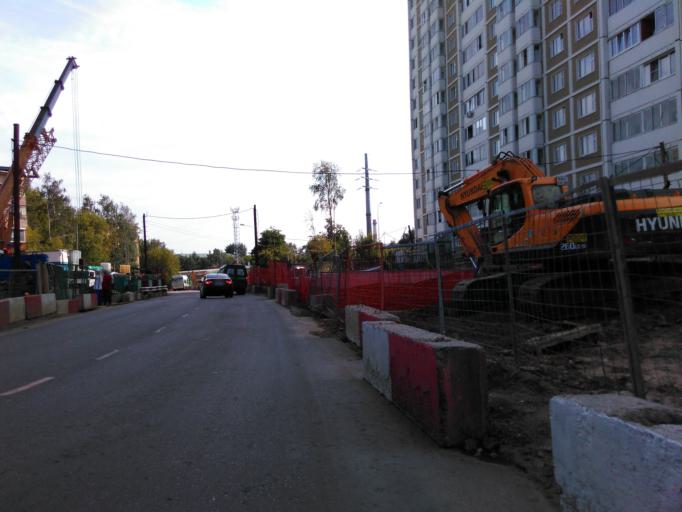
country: RU
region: Moskovskaya
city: Bol'shaya Setun'
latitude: 55.7117
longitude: 37.4044
